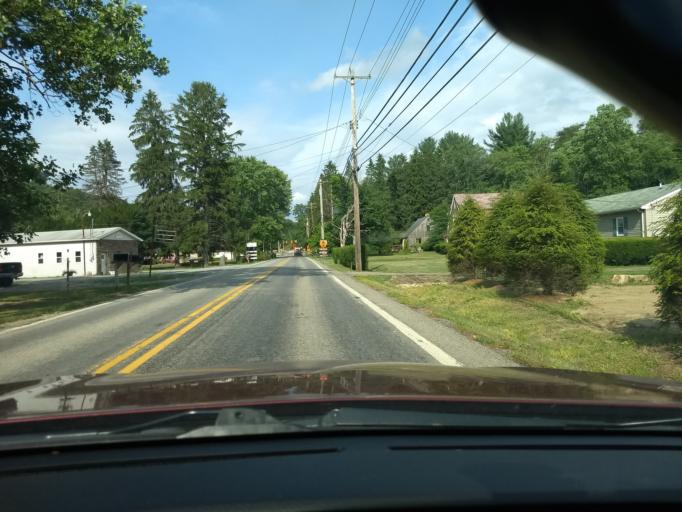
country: US
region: Pennsylvania
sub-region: Allegheny County
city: Bell Acres
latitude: 40.6079
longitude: -80.1621
